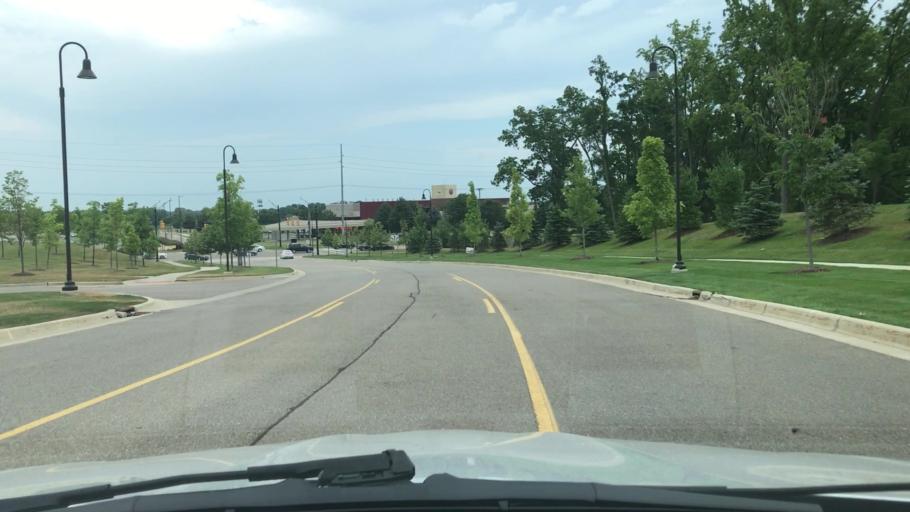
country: US
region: Michigan
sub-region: Wayne County
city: Northville
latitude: 42.4223
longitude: -83.4351
